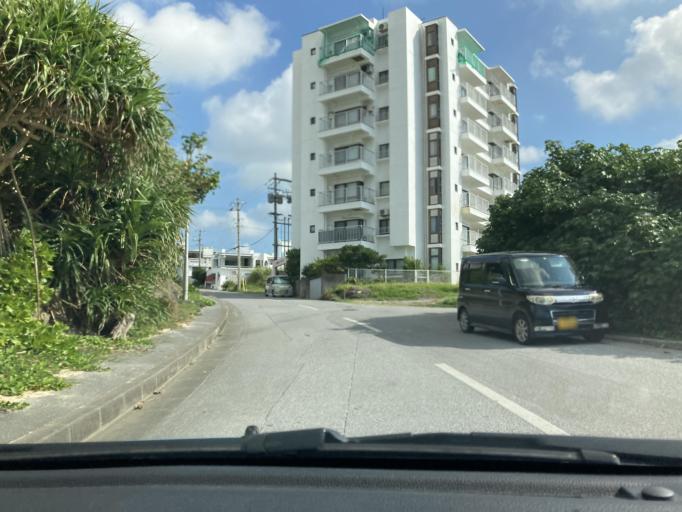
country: JP
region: Okinawa
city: Itoman
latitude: 26.1278
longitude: 127.7738
